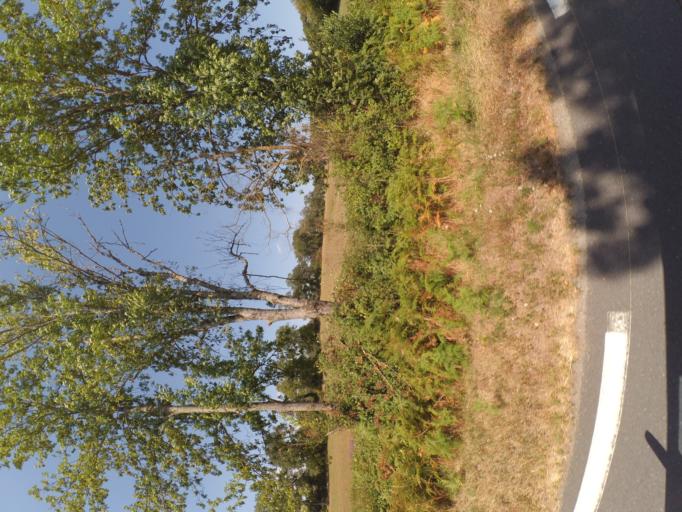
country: FR
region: Limousin
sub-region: Departement de la Haute-Vienne
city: Magnac-Laval
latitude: 46.2157
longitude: 1.1263
